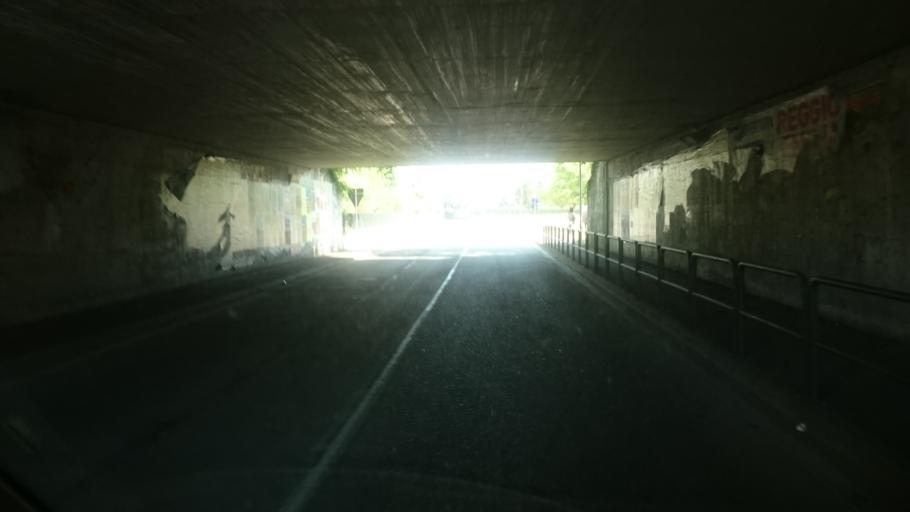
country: IT
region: Emilia-Romagna
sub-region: Provincia di Reggio Emilia
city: Scandiano
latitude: 44.6029
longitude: 10.6887
